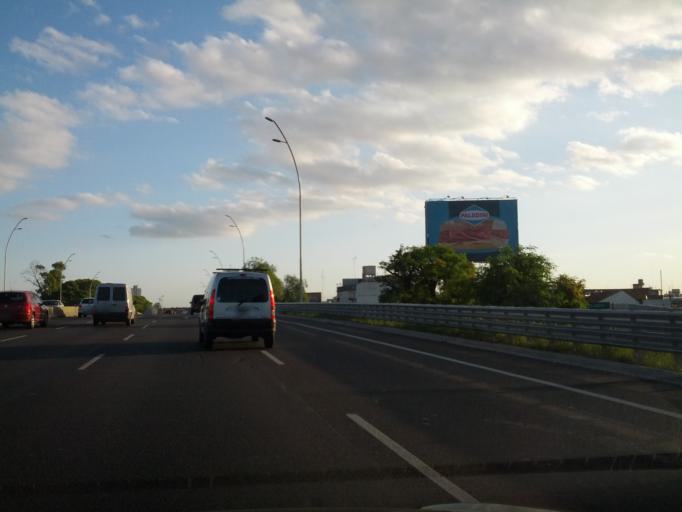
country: AR
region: Buenos Aires
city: Caseros
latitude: -34.6246
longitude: -58.5306
